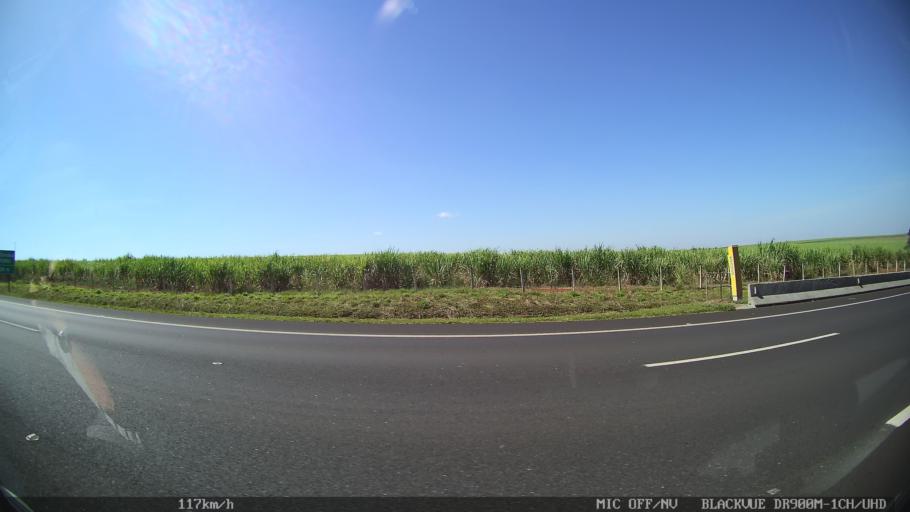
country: BR
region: Sao Paulo
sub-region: Franca
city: Franca
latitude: -20.6852
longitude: -47.4966
